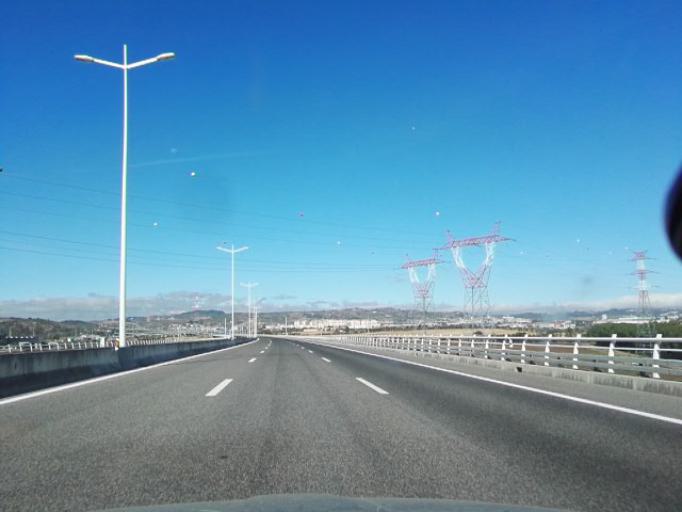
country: PT
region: Lisbon
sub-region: Alenquer
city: Carregado
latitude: 39.0159
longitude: -8.9465
